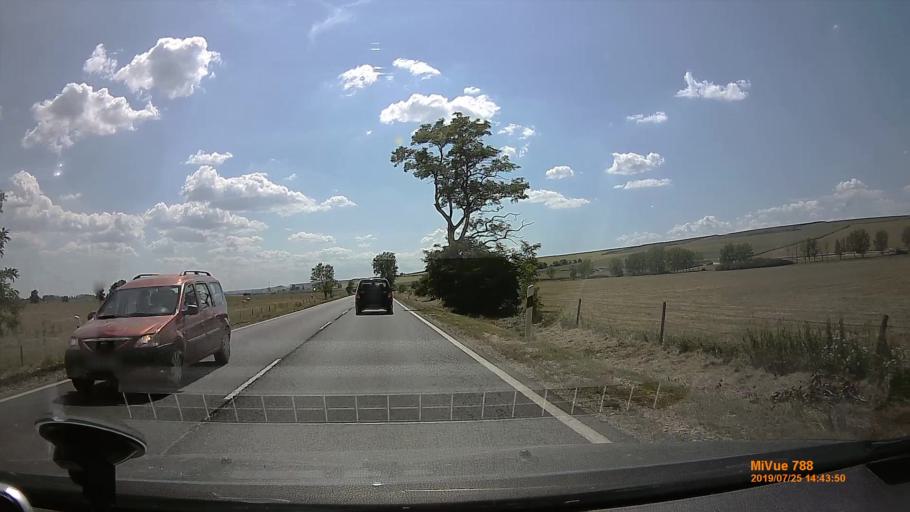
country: HU
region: Borsod-Abauj-Zemplen
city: Halmaj
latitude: 48.2707
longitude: 21.0065
